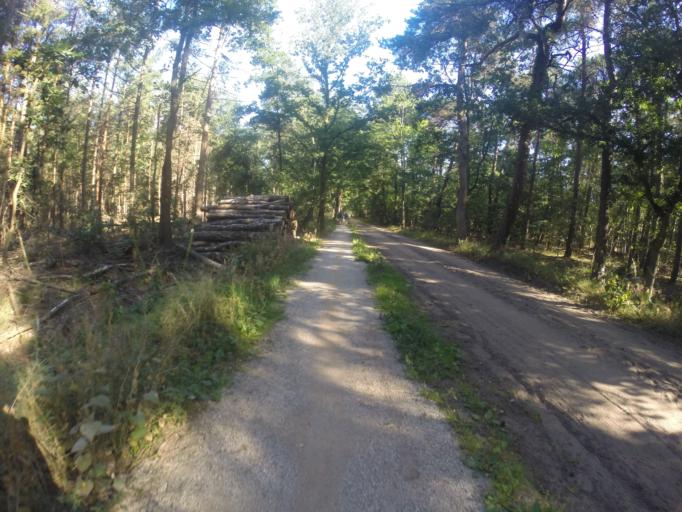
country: NL
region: Gelderland
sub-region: Gemeente Lochem
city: Almen
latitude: 52.1178
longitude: 6.3343
